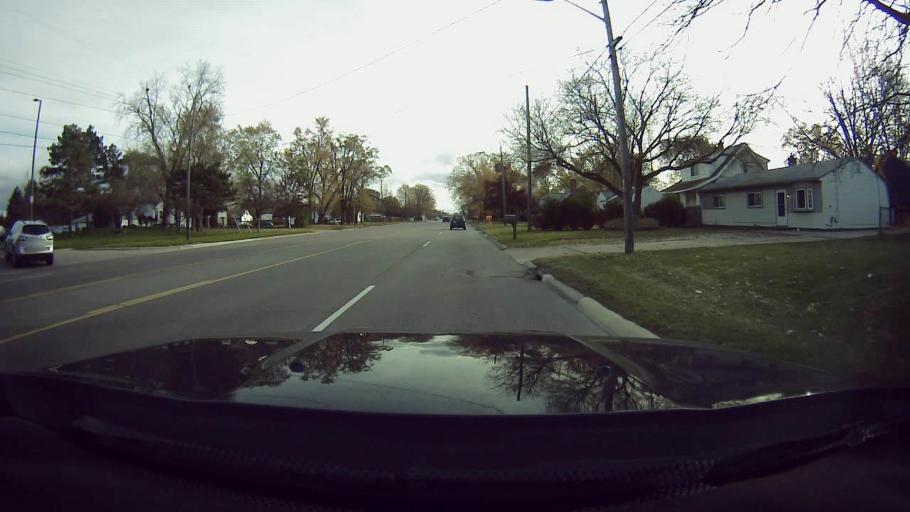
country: US
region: Michigan
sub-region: Macomb County
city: Eastpointe
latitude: 42.4793
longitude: -82.9724
